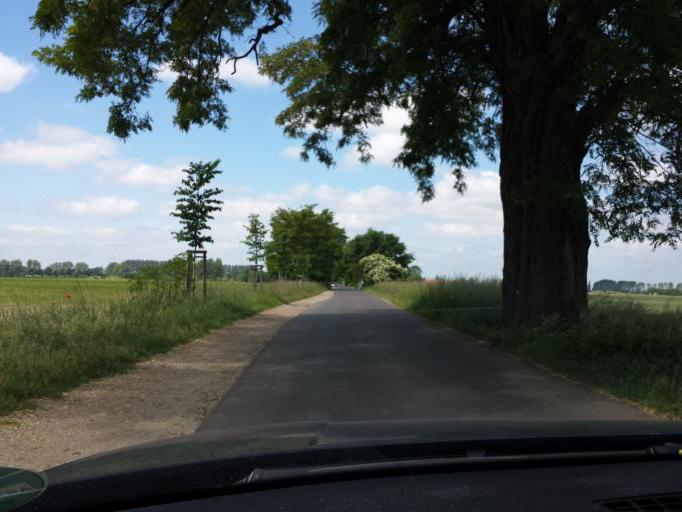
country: DE
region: Brandenburg
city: Ruthnick
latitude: 52.8218
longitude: 12.9886
